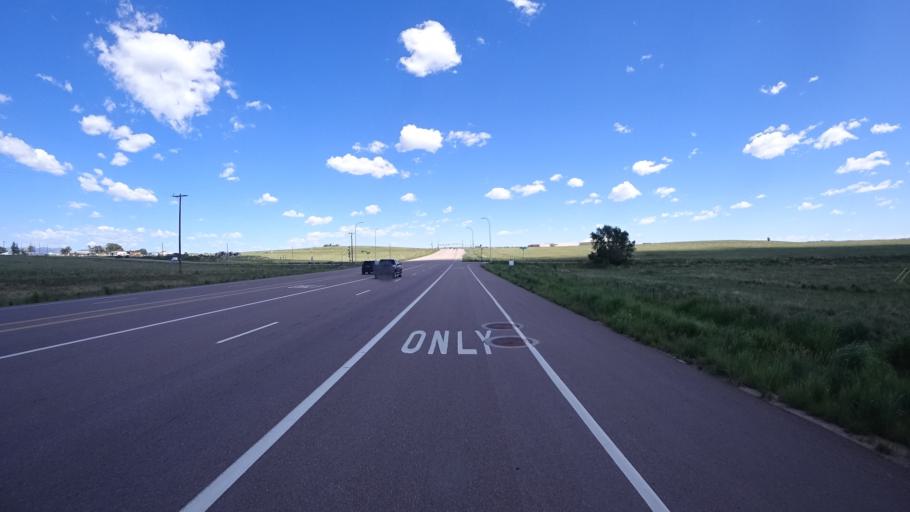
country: US
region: Colorado
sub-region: El Paso County
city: Cimarron Hills
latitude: 38.8371
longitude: -104.6826
